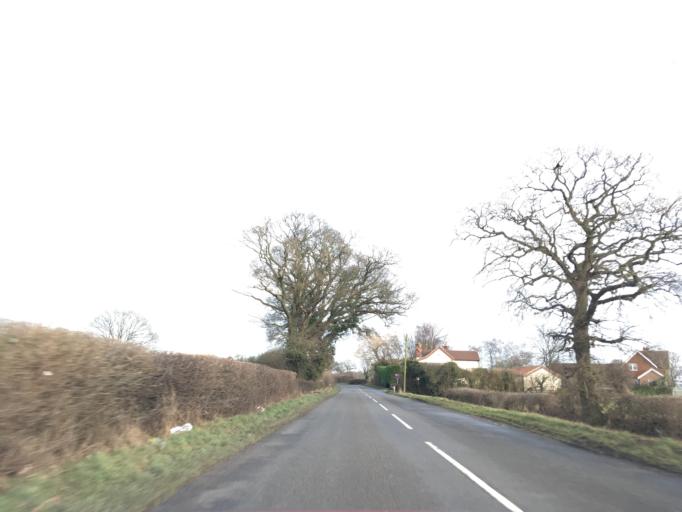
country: GB
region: England
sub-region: Nottinghamshire
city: South Collingham
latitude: 53.1821
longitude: -0.7512
